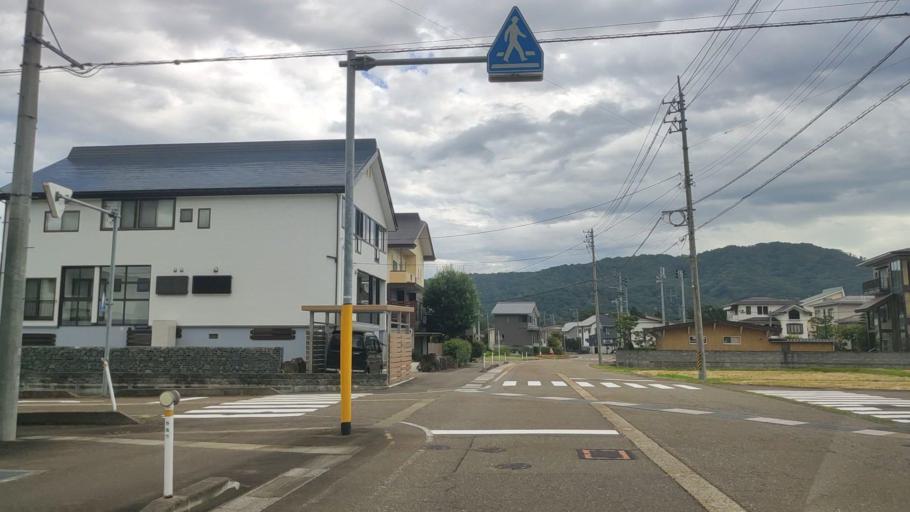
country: JP
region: Niigata
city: Arai
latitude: 37.0102
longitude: 138.2581
